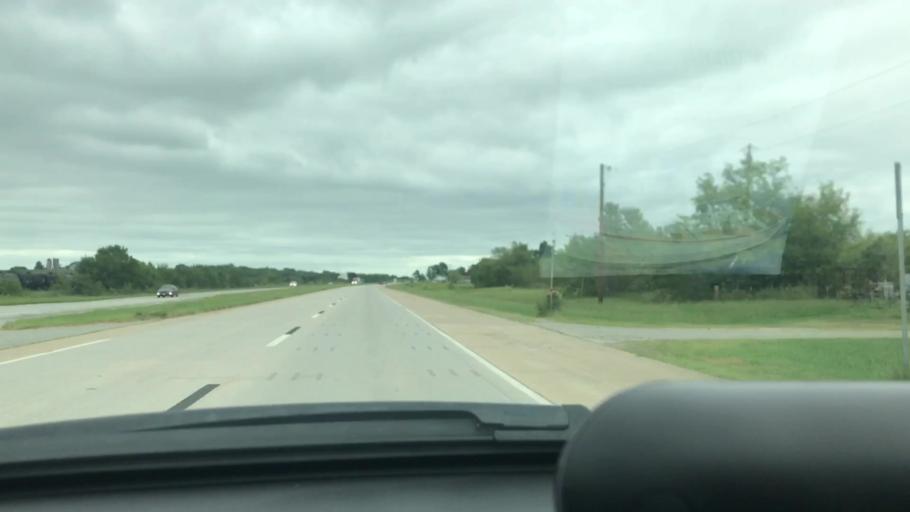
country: US
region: Oklahoma
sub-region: Mayes County
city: Chouteau
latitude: 36.0934
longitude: -95.3633
